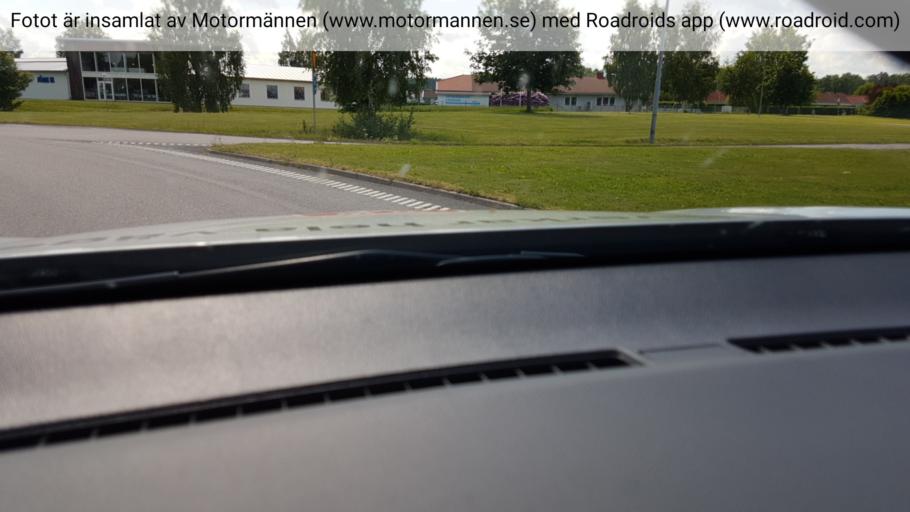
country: SE
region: Vaestra Goetaland
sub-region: Lidkopings Kommun
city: Lidkoping
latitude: 58.5030
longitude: 13.1254
